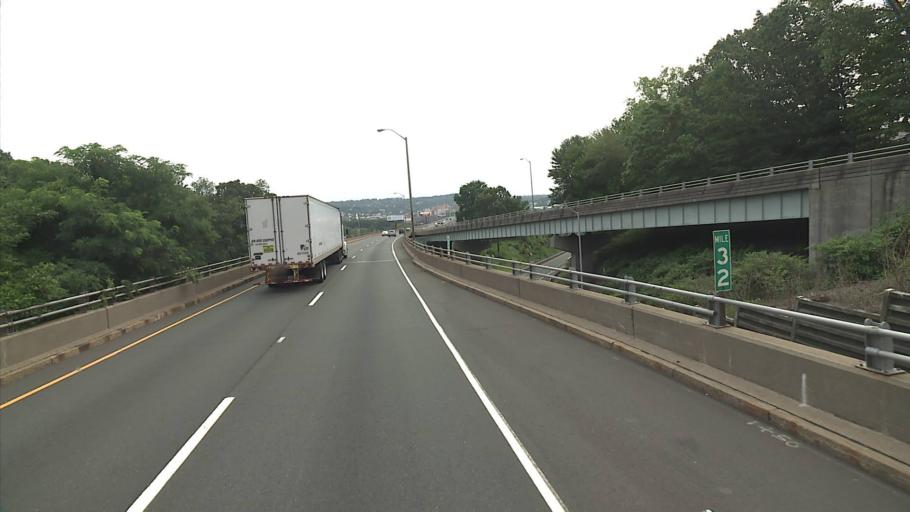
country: US
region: Connecticut
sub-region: New Haven County
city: Waterbury
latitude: 41.5512
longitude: -73.0552
